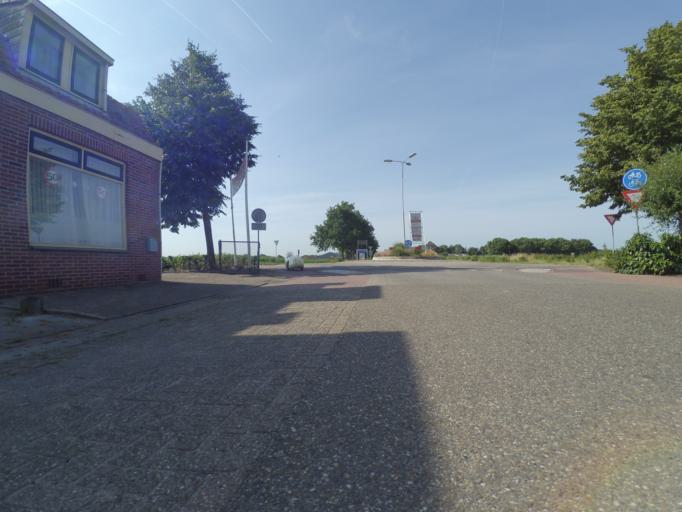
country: NL
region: North Brabant
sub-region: Gemeente Steenbergen
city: Welberg
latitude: 51.5384
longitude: 4.3423
